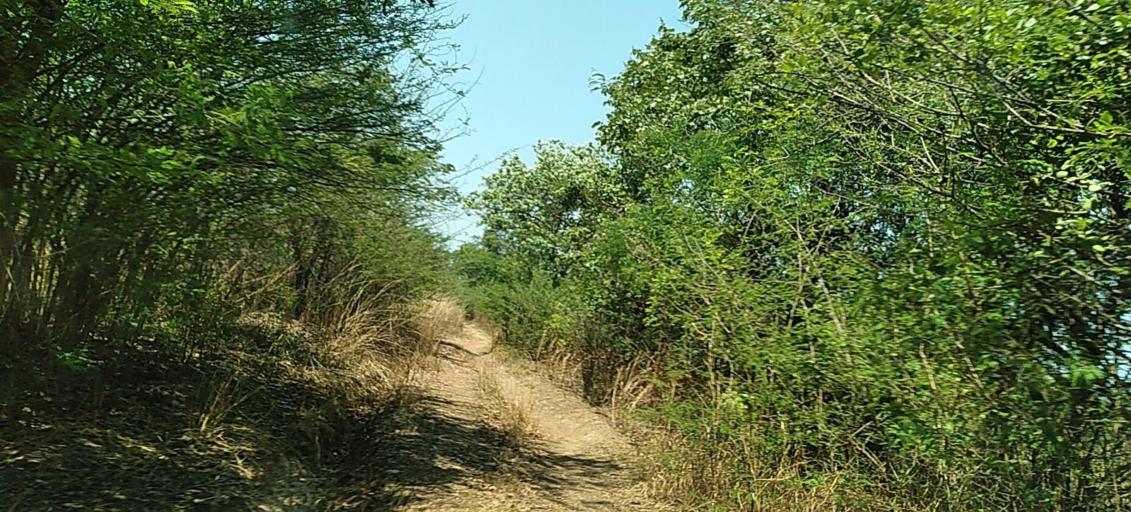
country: ZM
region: Copperbelt
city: Luanshya
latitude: -12.9893
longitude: 28.3257
